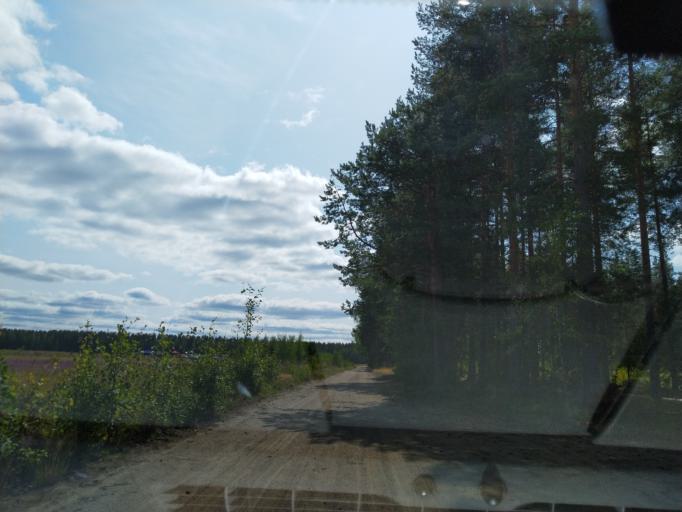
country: FI
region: Uusimaa
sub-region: Helsinki
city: Kaerkoelae
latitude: 60.7461
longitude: 24.1026
